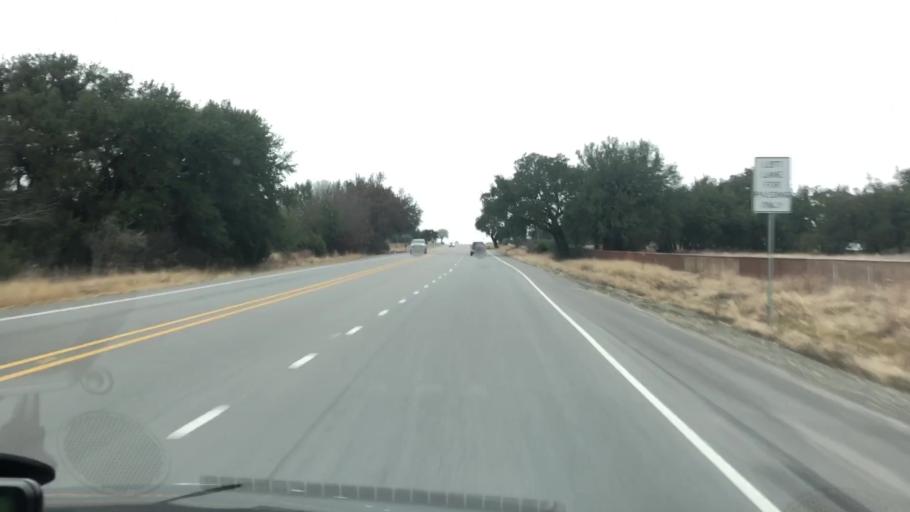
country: US
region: Texas
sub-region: Hamilton County
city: Hico
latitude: 32.0004
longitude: -98.0511
